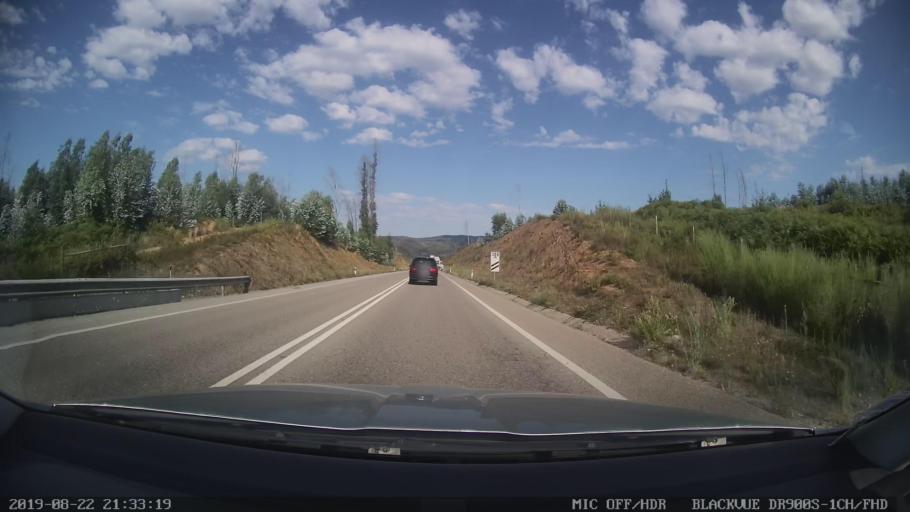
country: PT
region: Leiria
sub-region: Pedrogao Grande
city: Pedrogao Grande
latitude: 39.9264
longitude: -8.1760
